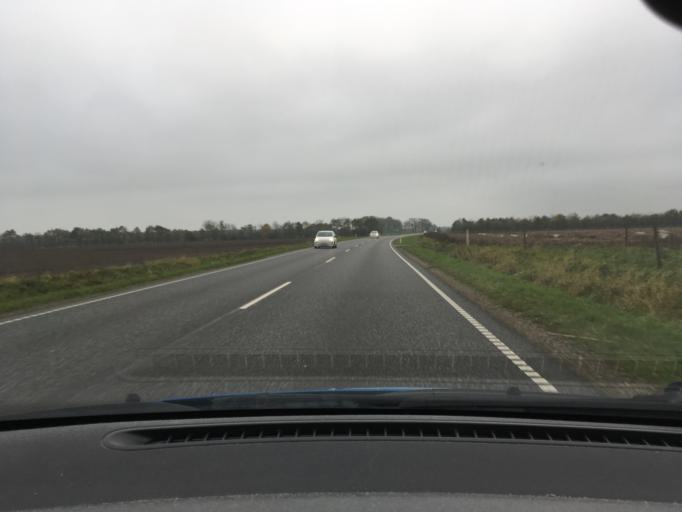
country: DK
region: South Denmark
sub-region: Tonder Kommune
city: Toftlund
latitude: 55.0639
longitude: 9.1479
